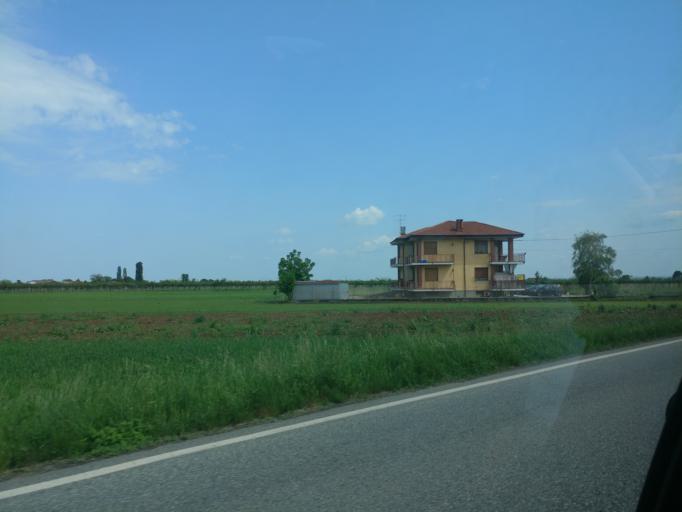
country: IT
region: Piedmont
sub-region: Provincia di Torino
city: Cavour
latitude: 44.7747
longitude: 7.3882
